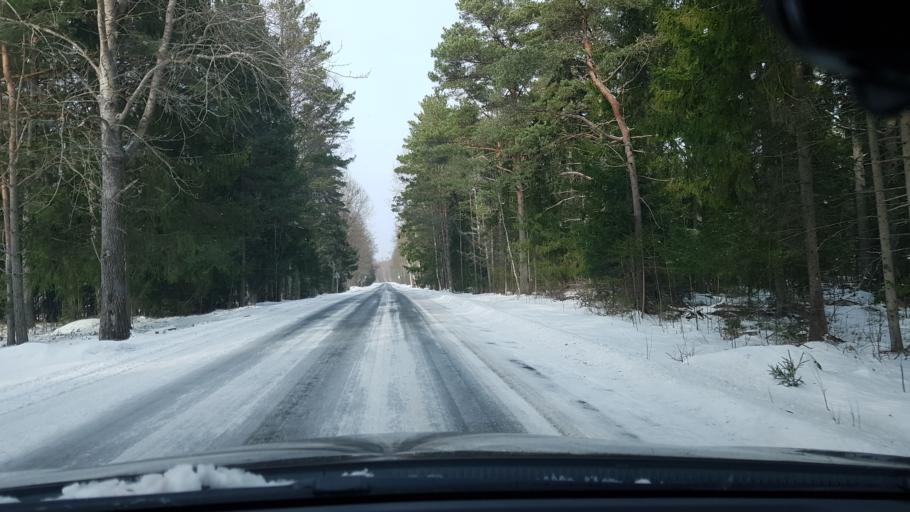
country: EE
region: Harju
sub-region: Kuusalu vald
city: Kuusalu
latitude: 59.5634
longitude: 25.5351
